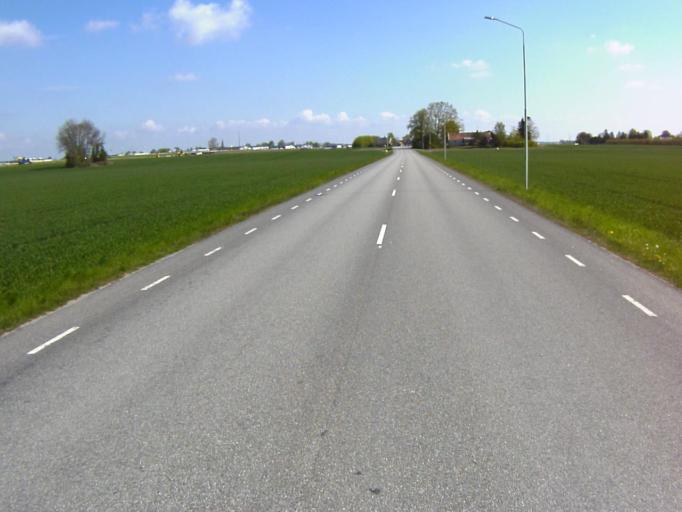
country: SE
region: Skane
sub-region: Kristianstads Kommun
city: Kristianstad
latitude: 56.0209
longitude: 14.2073
